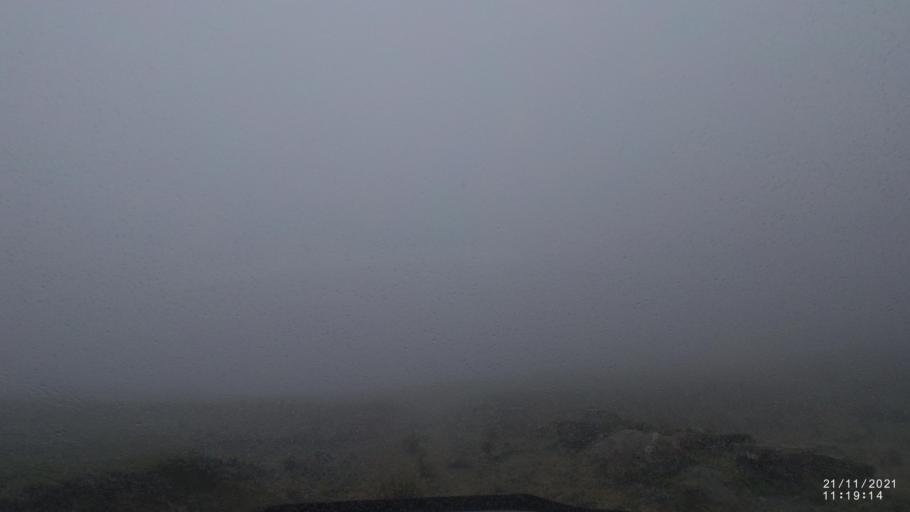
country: BO
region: Cochabamba
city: Cochabamba
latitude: -16.9617
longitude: -66.2691
